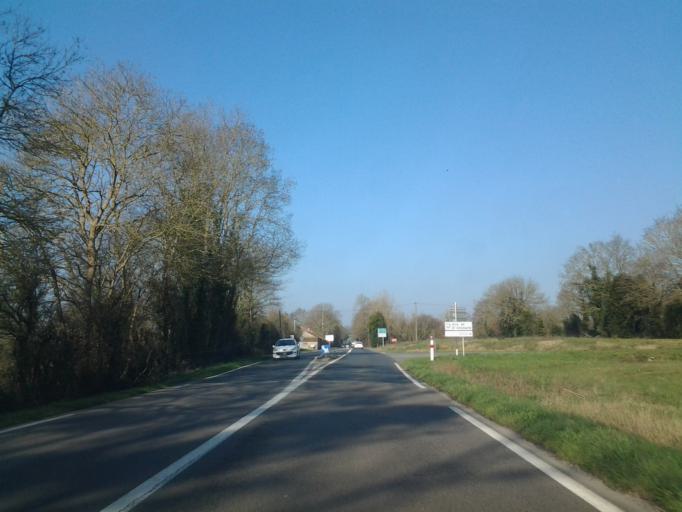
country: FR
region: Pays de la Loire
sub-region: Departement de la Vendee
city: Saint-Christophe-du-Ligneron
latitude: 46.8155
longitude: -1.7551
